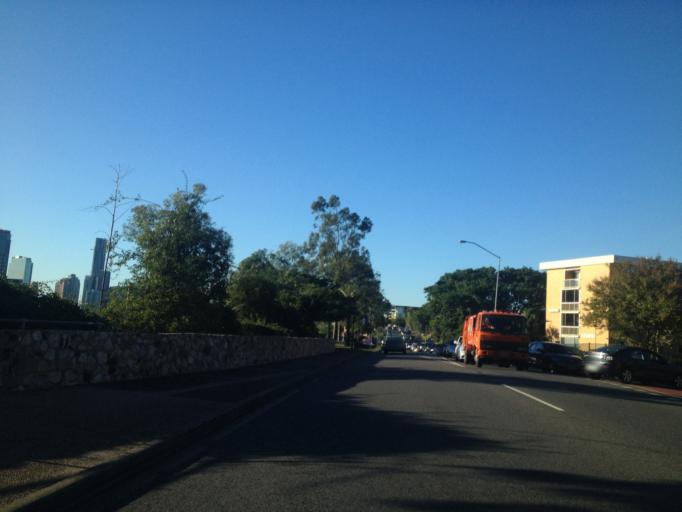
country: AU
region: Queensland
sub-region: Brisbane
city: Woolloongabba
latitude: -27.4808
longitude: 153.0333
